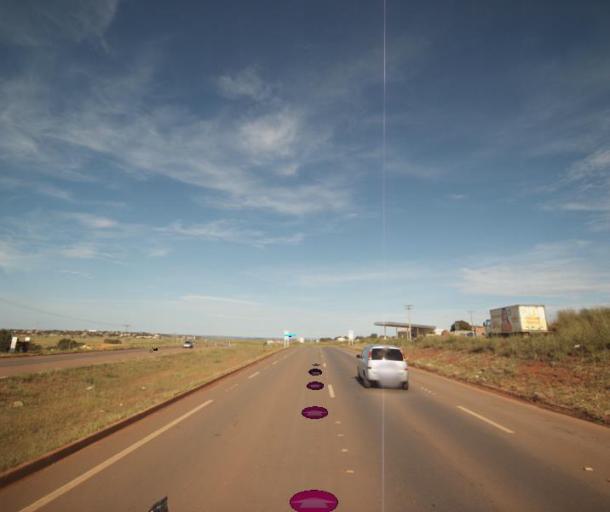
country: BR
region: Federal District
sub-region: Brasilia
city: Brasilia
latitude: -15.7410
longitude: -48.3128
